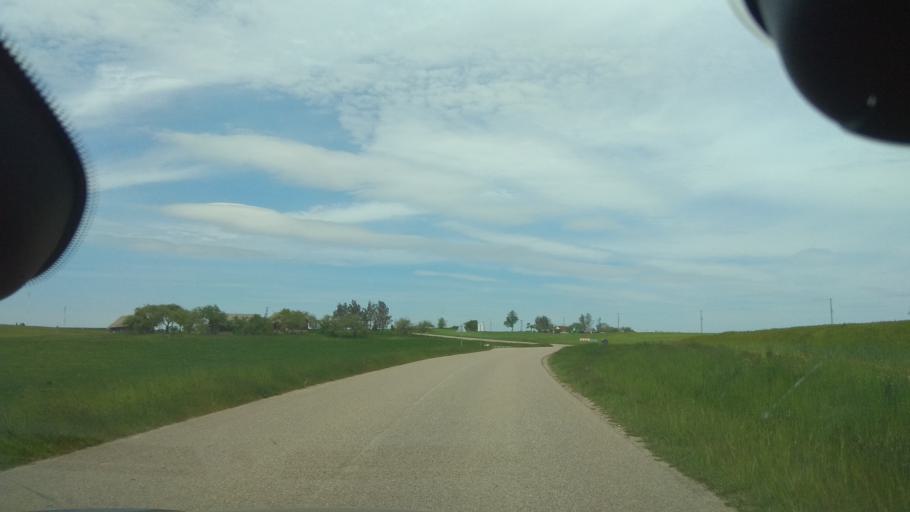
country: LT
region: Vilnius County
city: Ukmerge
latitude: 55.1590
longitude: 24.5430
